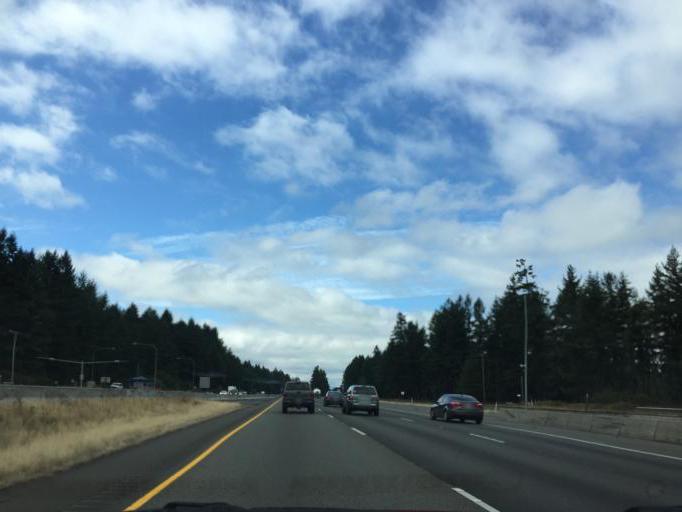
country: US
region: Washington
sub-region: Pierce County
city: DuPont
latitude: 47.0863
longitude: -122.6518
